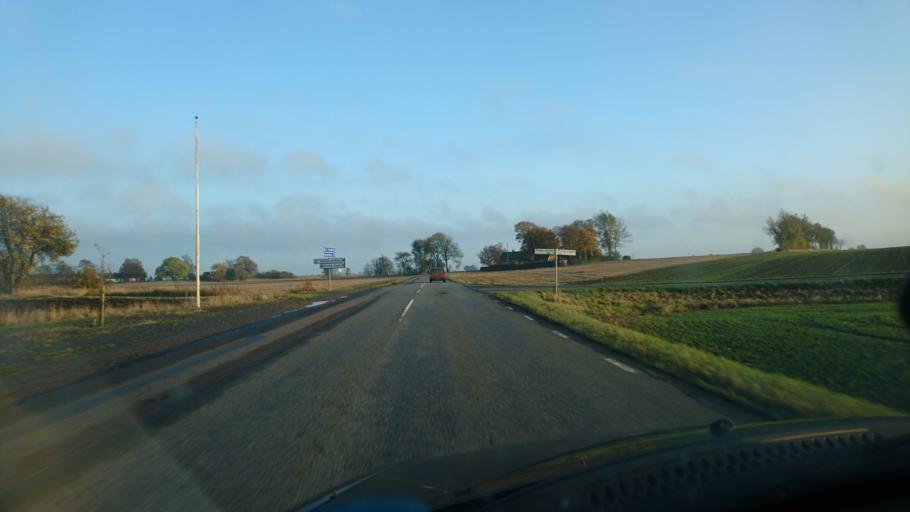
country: SE
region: Skane
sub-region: Tomelilla Kommun
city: Tomelilla
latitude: 55.4601
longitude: 14.1058
